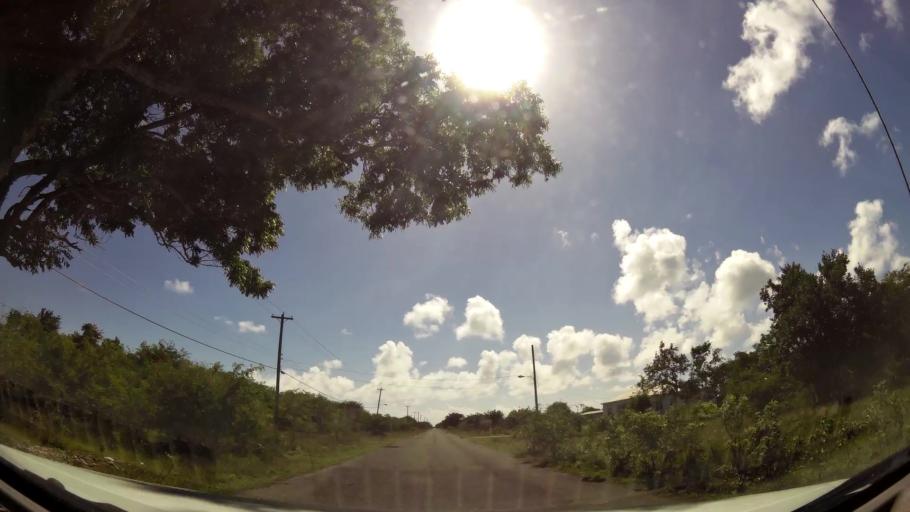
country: AG
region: Barbuda
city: Codrington
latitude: 17.6187
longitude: -61.8282
